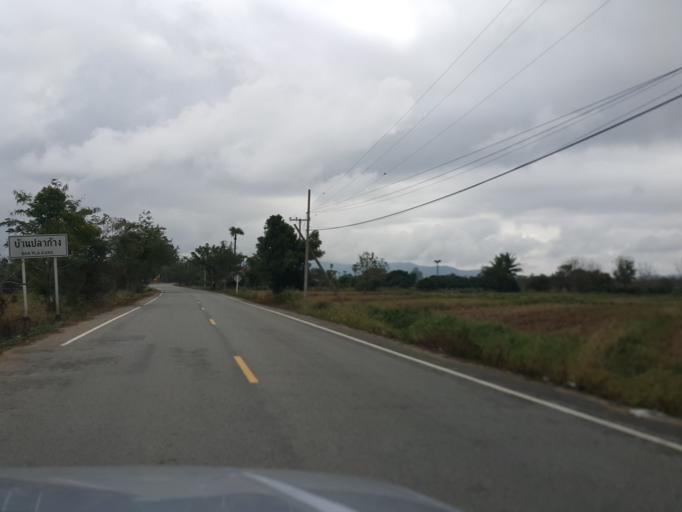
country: TH
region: Lamphun
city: Ban Thi
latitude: 18.6792
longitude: 99.1402
